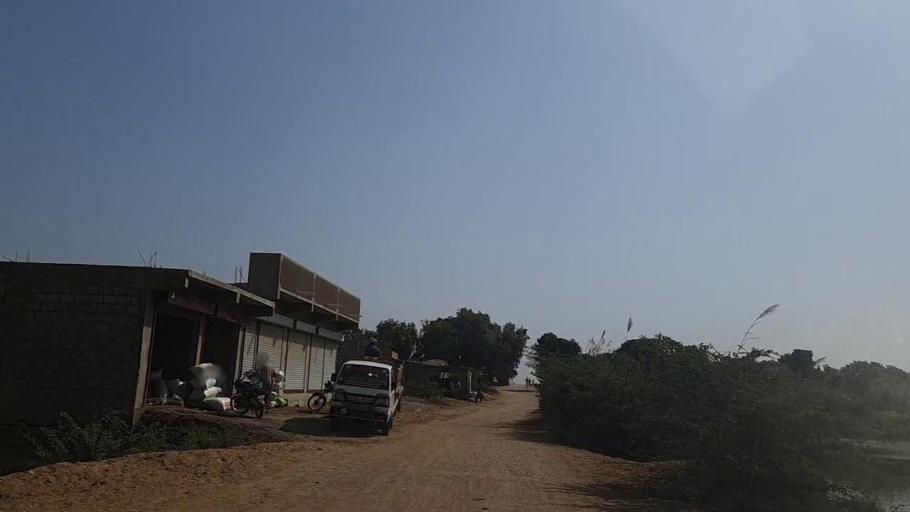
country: PK
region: Sindh
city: Daro Mehar
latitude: 24.7221
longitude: 68.0736
